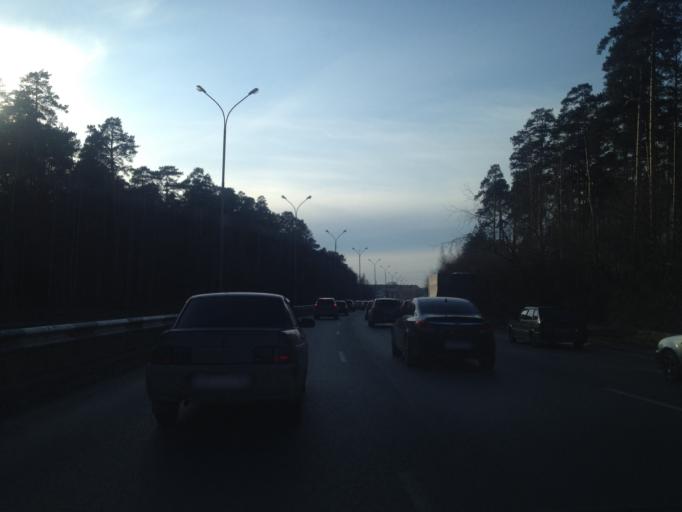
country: RU
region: Sverdlovsk
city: Sovkhoznyy
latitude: 56.7891
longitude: 60.5804
